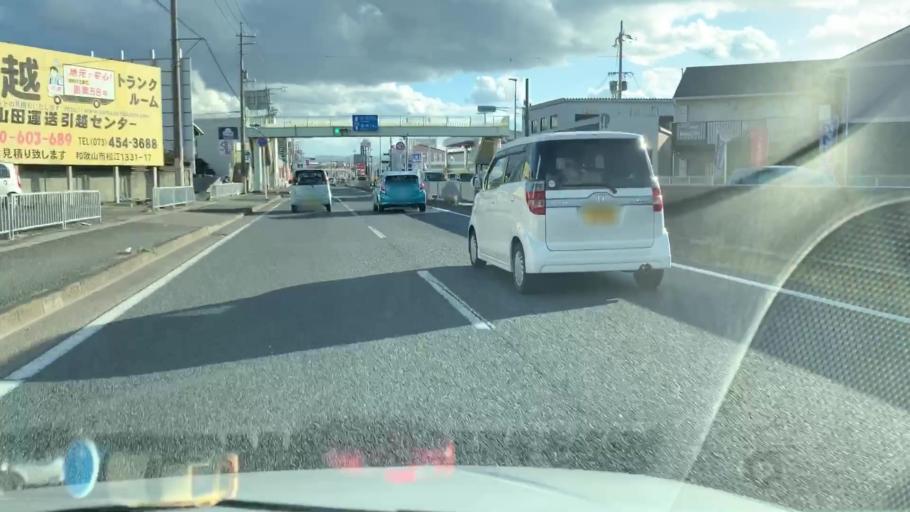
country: JP
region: Wakayama
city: Wakayama-shi
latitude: 34.2473
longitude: 135.1501
